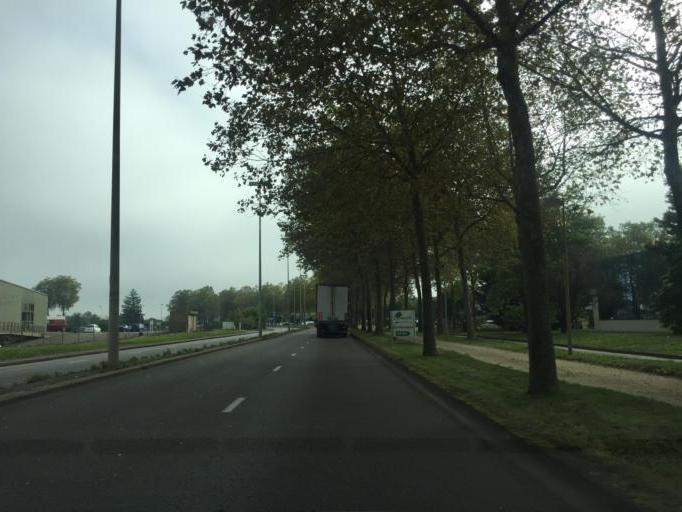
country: FR
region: Rhone-Alpes
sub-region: Departement de l'Ain
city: Bourg-en-Bresse
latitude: 46.1950
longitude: 5.2329
